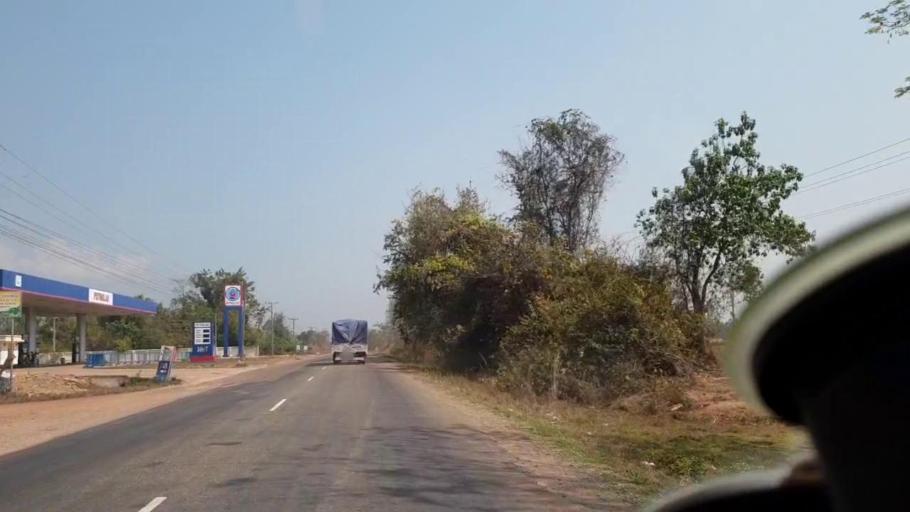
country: TH
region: Nong Khai
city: Phon Phisai
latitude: 18.0970
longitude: 103.0169
